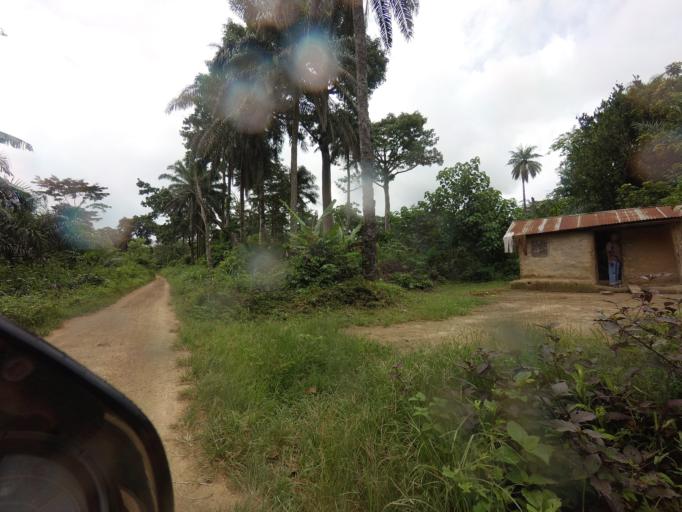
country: SL
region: Eastern Province
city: Buedu
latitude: 8.2950
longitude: -10.3640
